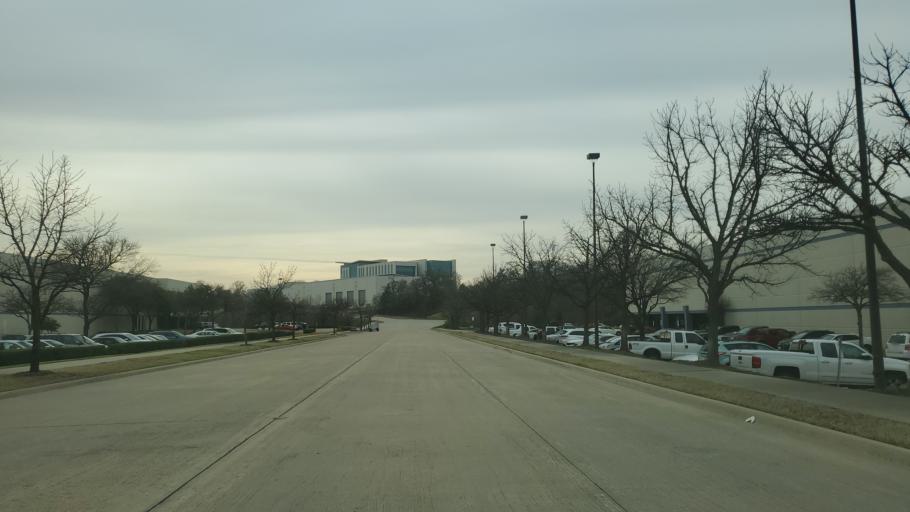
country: US
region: Texas
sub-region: Dallas County
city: Coppell
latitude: 32.9824
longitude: -97.0262
